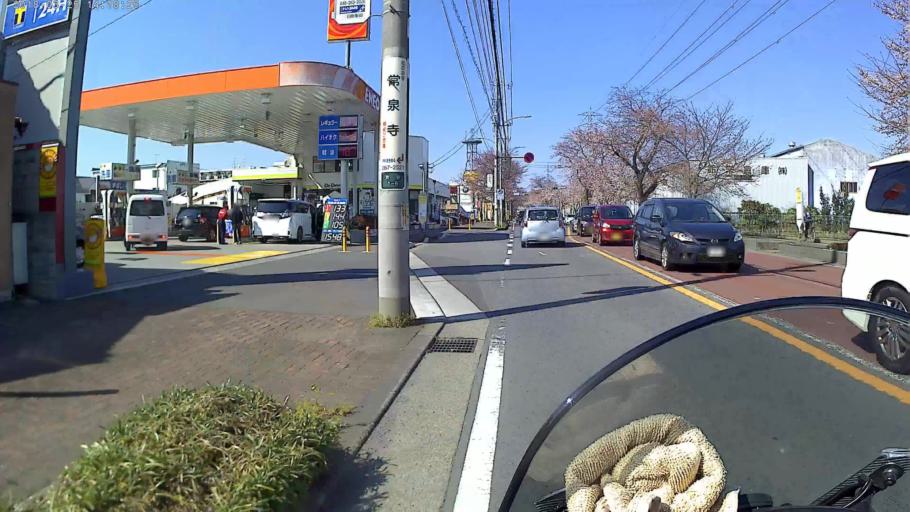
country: JP
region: Kanagawa
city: Minami-rinkan
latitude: 35.4366
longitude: 139.4668
